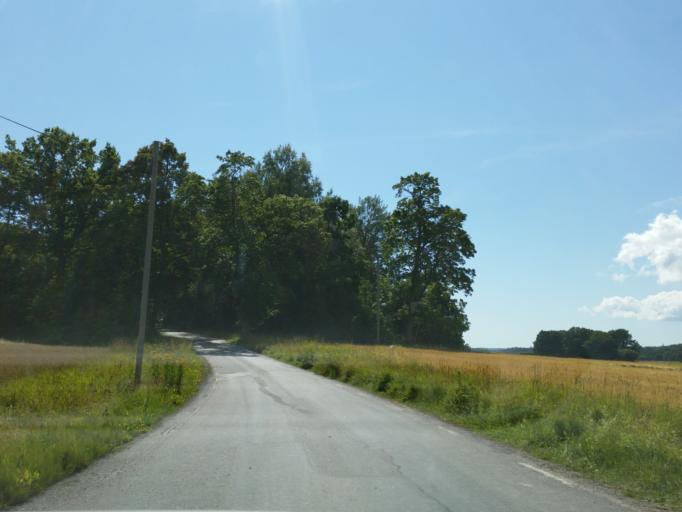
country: SE
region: Soedermanland
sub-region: Trosa Kommun
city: Trosa
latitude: 58.9827
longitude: 17.6549
